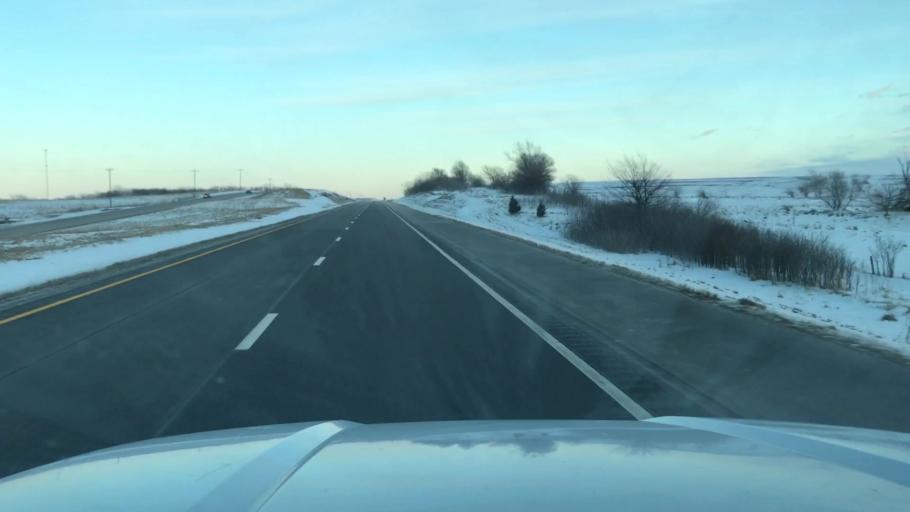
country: US
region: Missouri
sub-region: Clinton County
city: Gower
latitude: 39.7619
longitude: -94.5326
